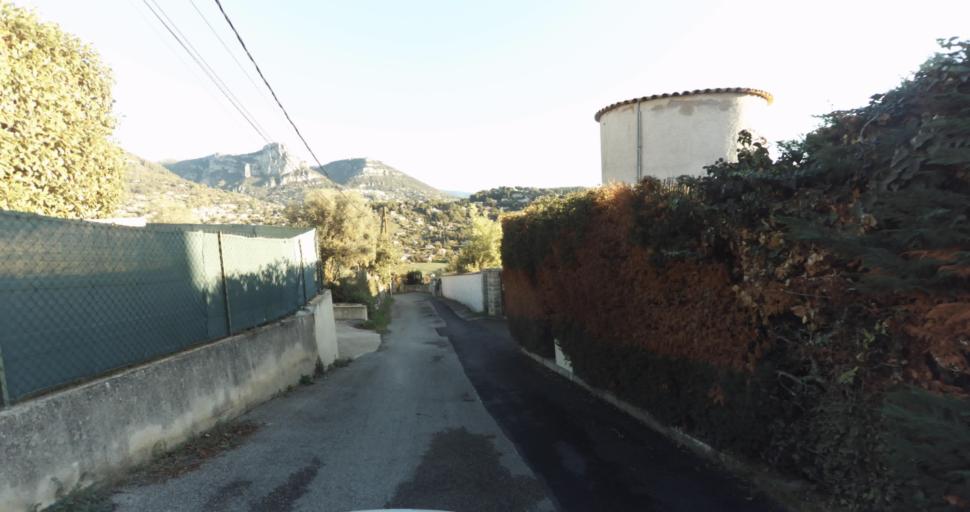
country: FR
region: Provence-Alpes-Cote d'Azur
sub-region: Departement des Alpes-Maritimes
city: Vence
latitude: 43.7220
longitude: 7.1240
